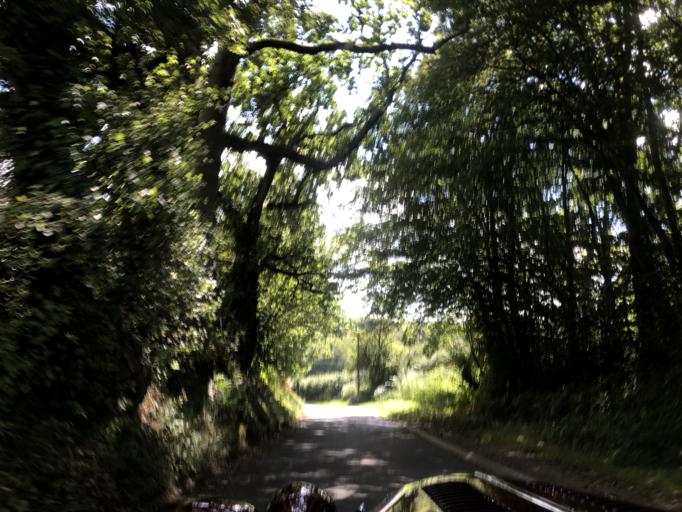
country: GB
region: England
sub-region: East Sussex
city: Northiam
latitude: 50.9944
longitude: 0.5700
